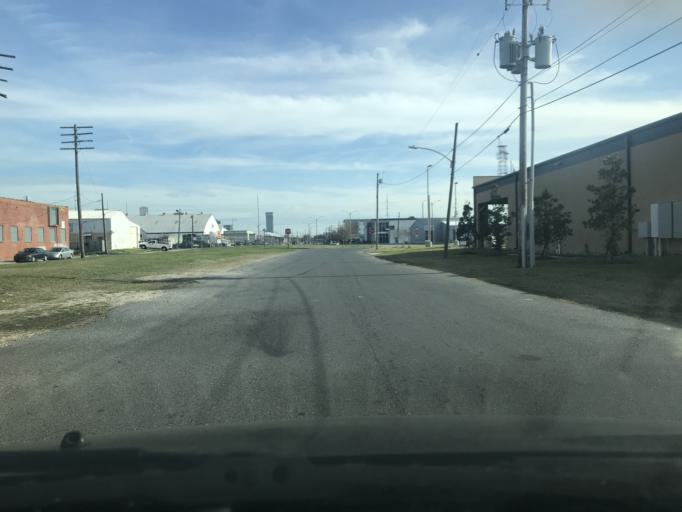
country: US
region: Louisiana
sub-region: Orleans Parish
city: New Orleans
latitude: 29.9582
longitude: -90.1020
